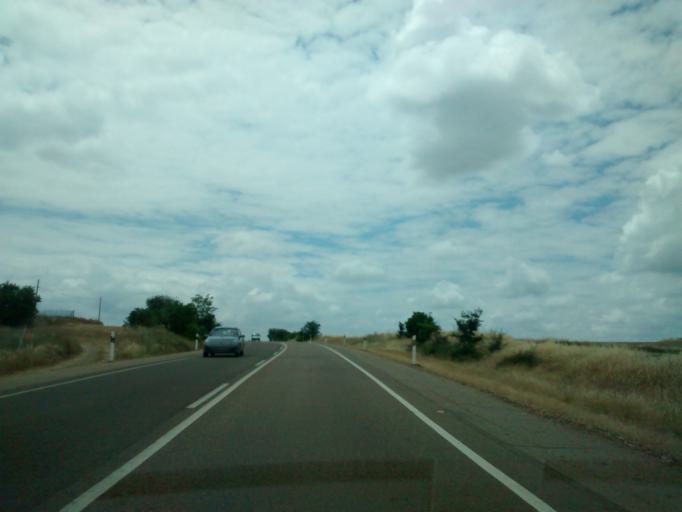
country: ES
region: Extremadura
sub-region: Provincia de Badajoz
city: Merida
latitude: 38.9328
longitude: -6.3111
